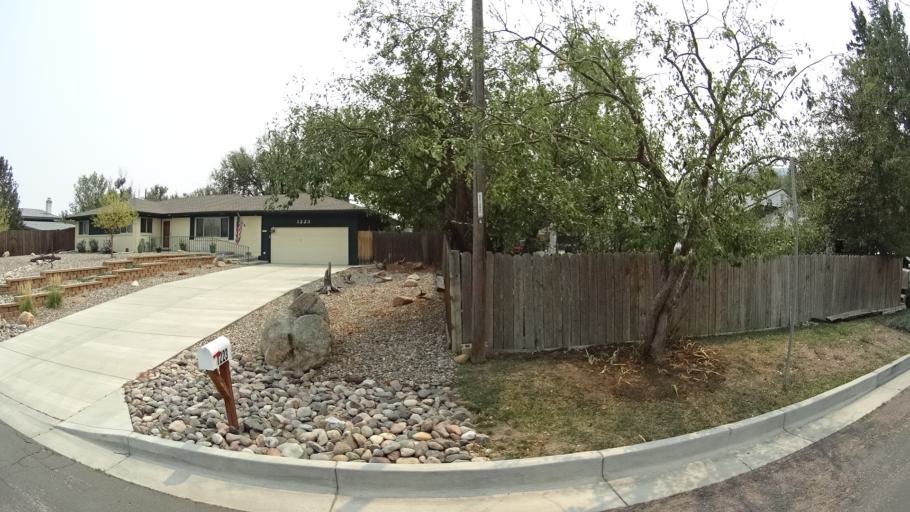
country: US
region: Colorado
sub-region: El Paso County
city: Colorado Springs
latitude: 38.8022
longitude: -104.8532
